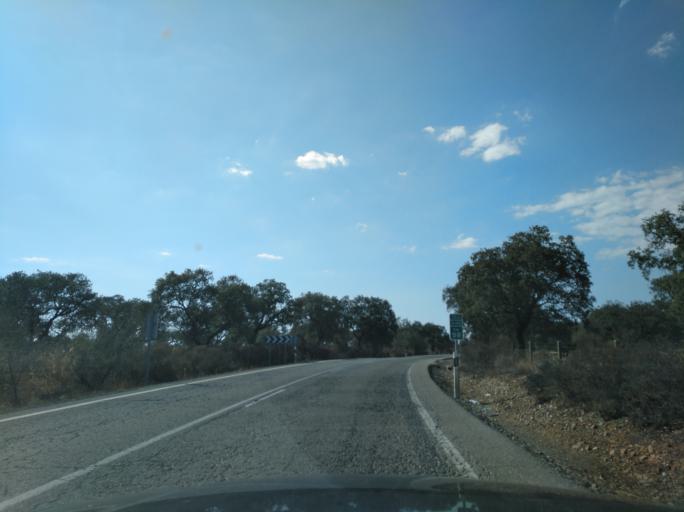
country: ES
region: Andalusia
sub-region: Provincia de Huelva
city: Santa Barbara de Casa
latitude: 37.7679
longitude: -7.1403
